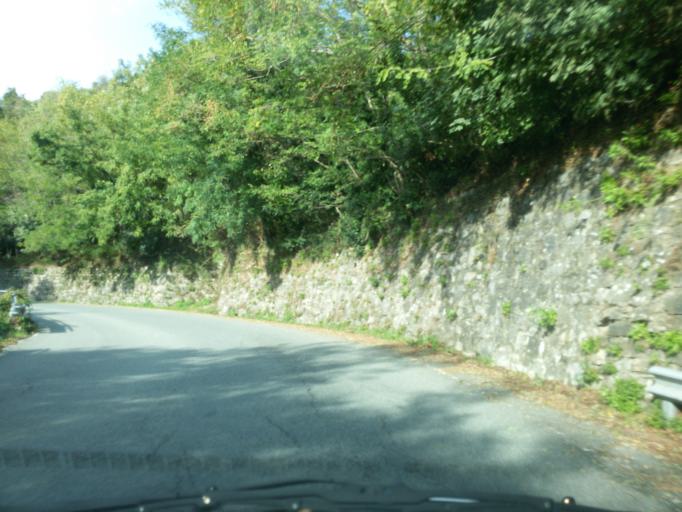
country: IT
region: Liguria
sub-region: Provincia di Genova
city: Piccarello
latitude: 44.4900
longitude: 8.9746
